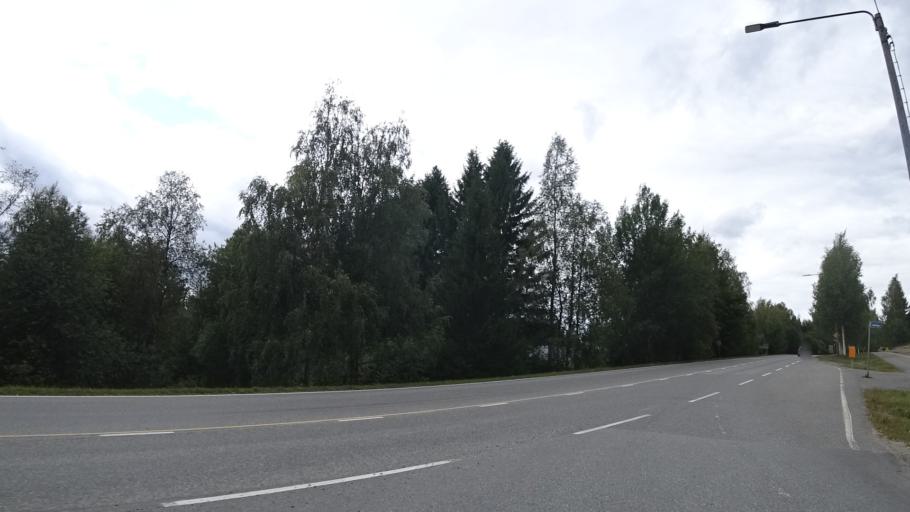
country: FI
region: North Karelia
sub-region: Joensuu
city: Ilomantsi
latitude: 62.6545
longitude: 30.9358
